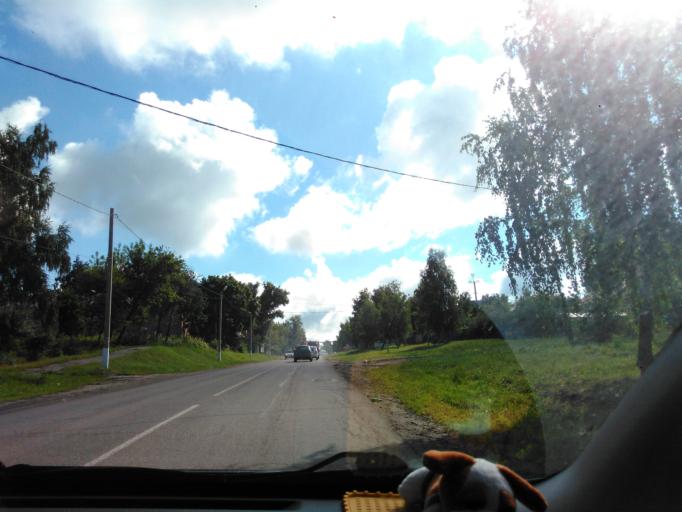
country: RU
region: Penza
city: Lermontovo
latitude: 53.1878
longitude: 44.0650
